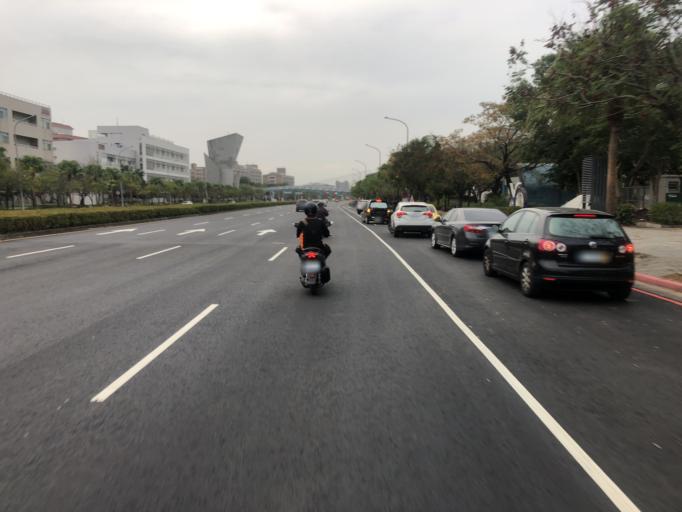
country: TW
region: Taiwan
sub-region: Tainan
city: Tainan
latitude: 23.1056
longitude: 120.2927
